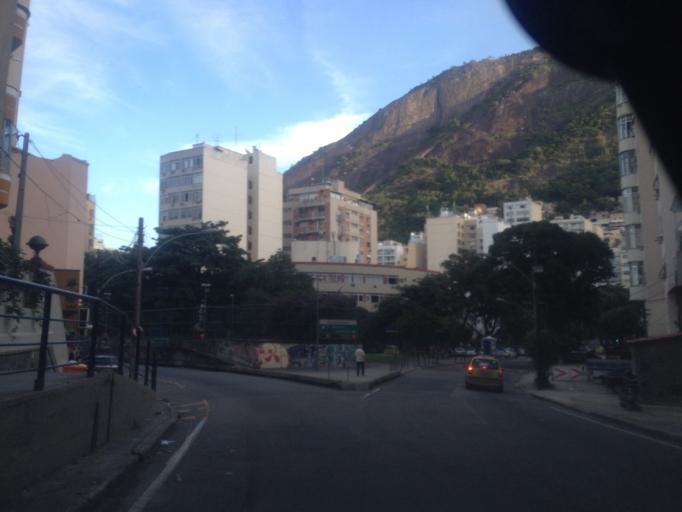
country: BR
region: Rio de Janeiro
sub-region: Rio De Janeiro
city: Rio de Janeiro
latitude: -22.9617
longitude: -43.1911
